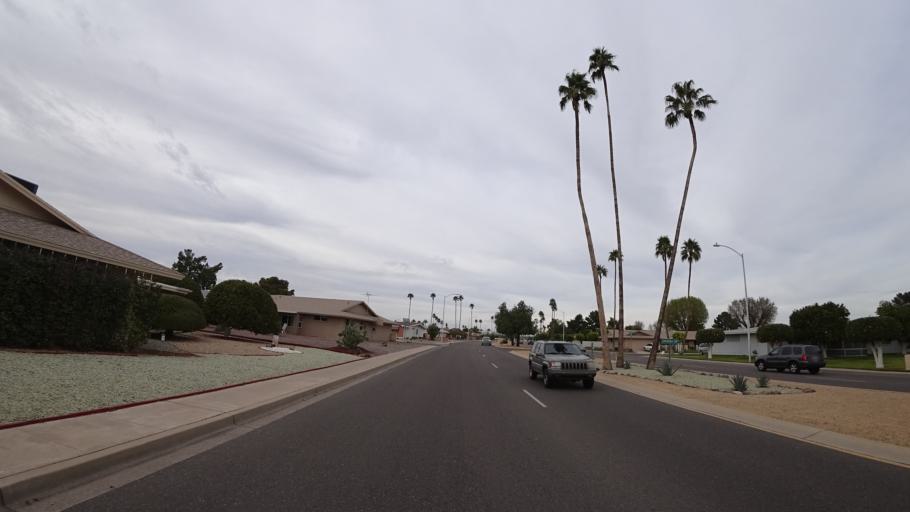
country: US
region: Arizona
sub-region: Maricopa County
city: Youngtown
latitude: 33.6136
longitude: -112.2907
